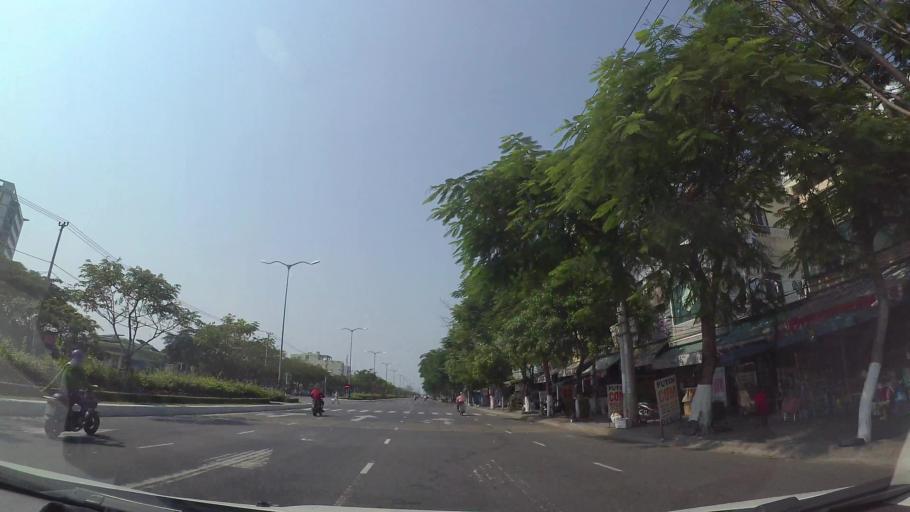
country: VN
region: Da Nang
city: Ngu Hanh Son
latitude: 16.0231
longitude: 108.2509
